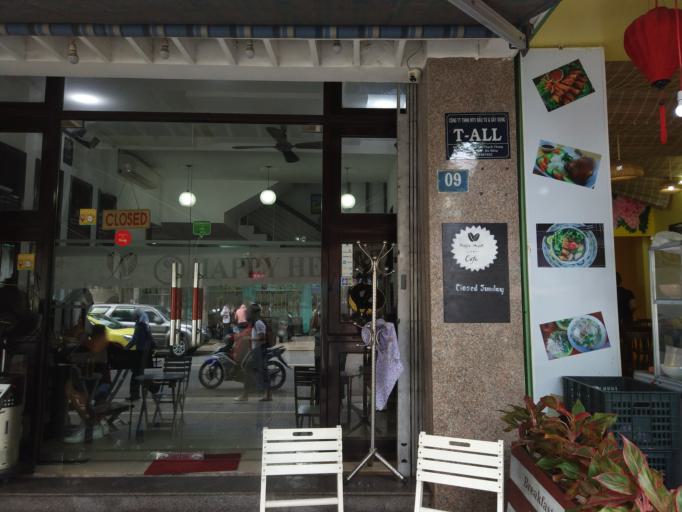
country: VN
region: Da Nang
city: Da Nang
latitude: 16.0776
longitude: 108.2210
